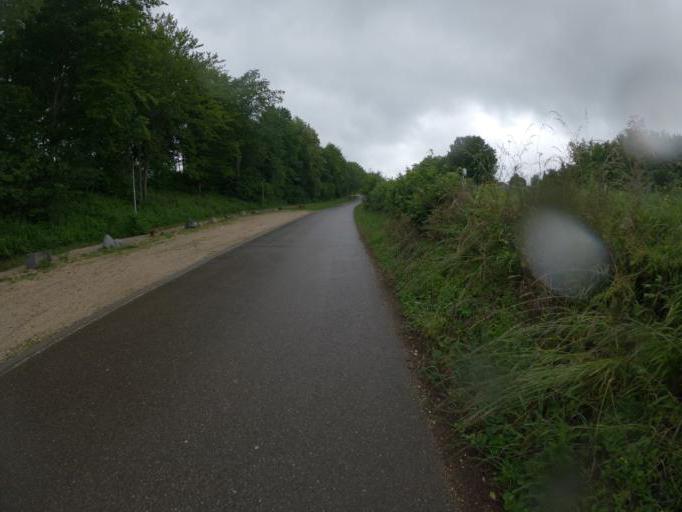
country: DE
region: Baden-Wuerttemberg
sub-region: Regierungsbezirk Stuttgart
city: Adelberg
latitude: 48.7612
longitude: 9.5945
